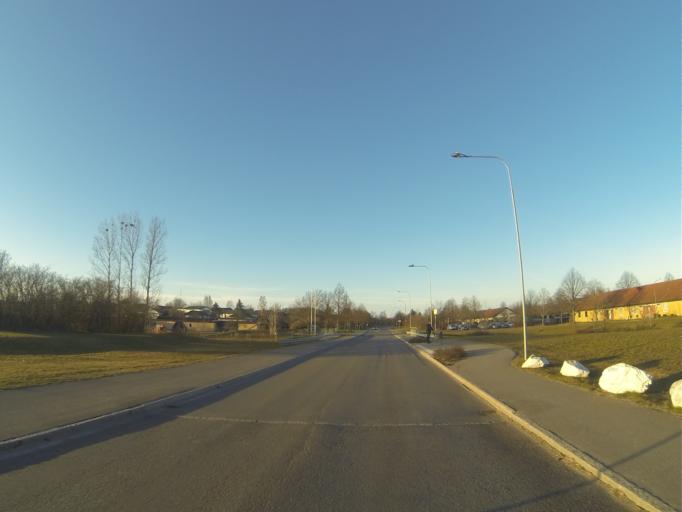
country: SE
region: Skane
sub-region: Svedala Kommun
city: Klagerup
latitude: 55.5790
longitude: 13.1789
